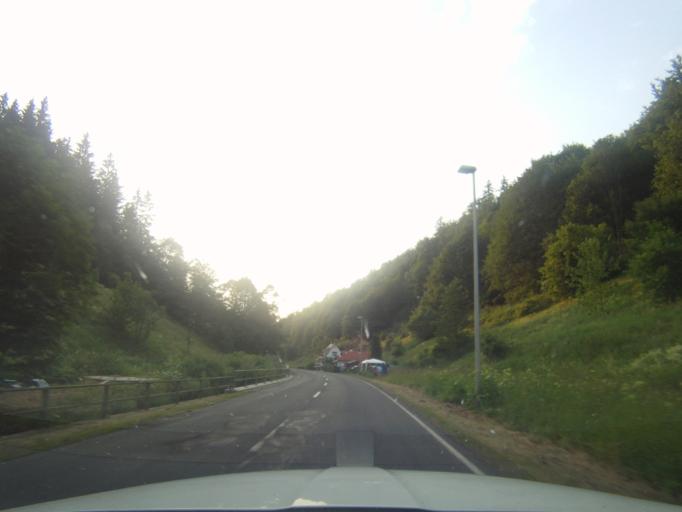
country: DE
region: Thuringia
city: Frauenwald
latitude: 50.4982
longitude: 10.8517
